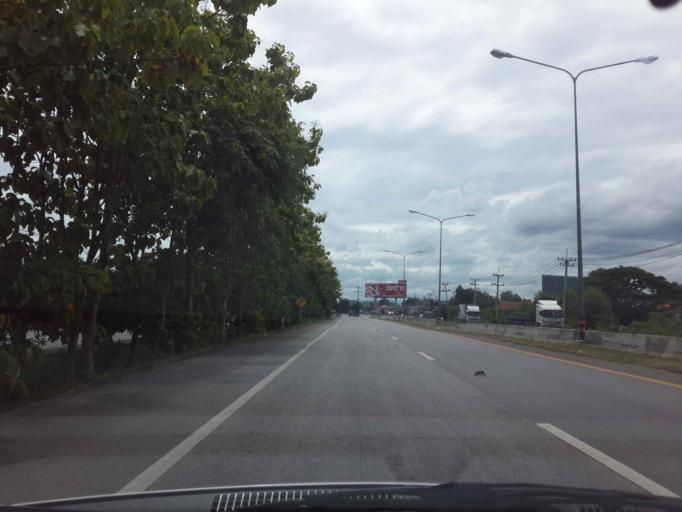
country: TH
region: Phetchaburi
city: Phetchaburi
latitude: 13.1251
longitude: 99.8793
